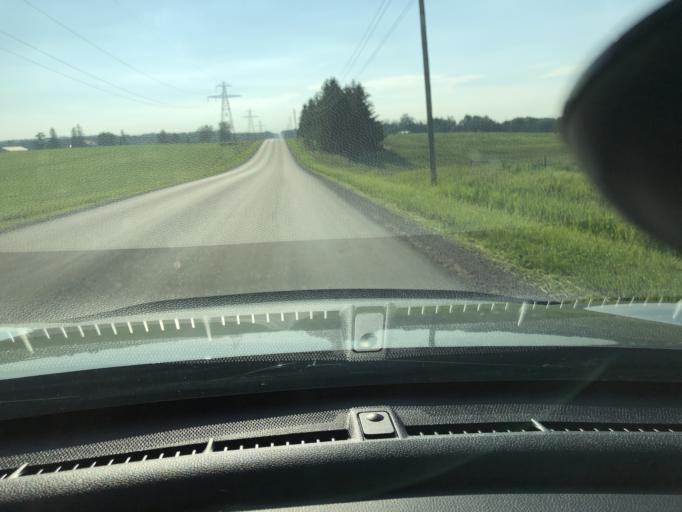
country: CA
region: Ontario
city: Stratford
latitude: 43.3884
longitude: -80.8838
